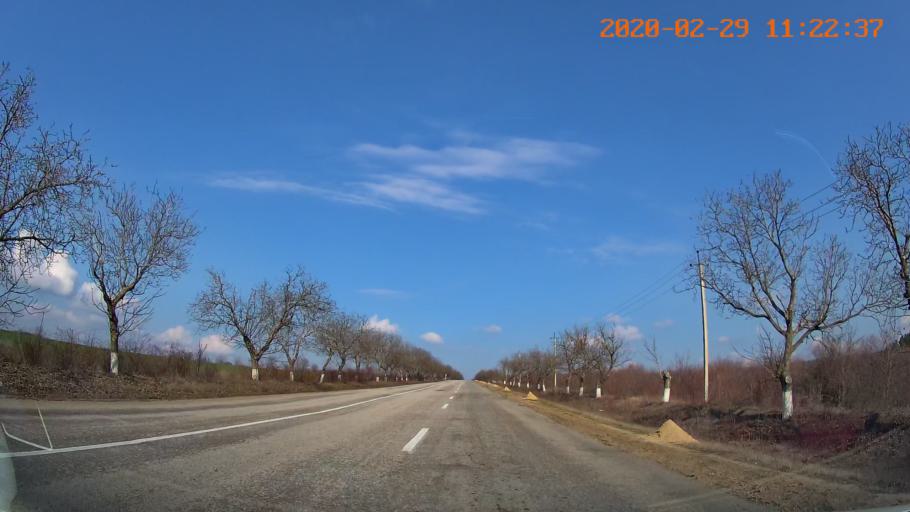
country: MD
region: Telenesti
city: Cocieri
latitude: 47.3964
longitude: 29.1615
